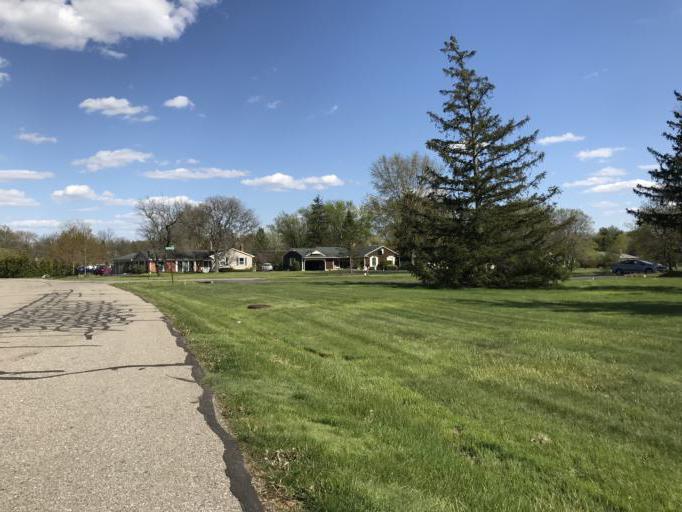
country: US
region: Michigan
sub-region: Oakland County
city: Farmington
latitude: 42.4755
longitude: -83.3300
